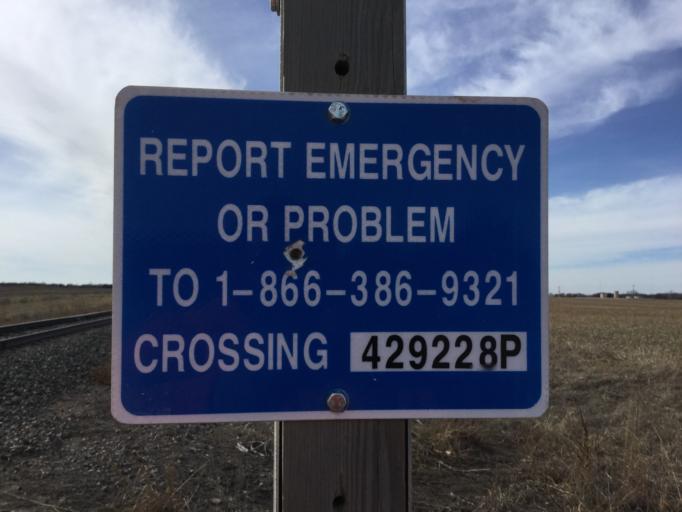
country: US
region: Kansas
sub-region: Barton County
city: Ellinwood
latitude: 38.5145
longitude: -98.4619
